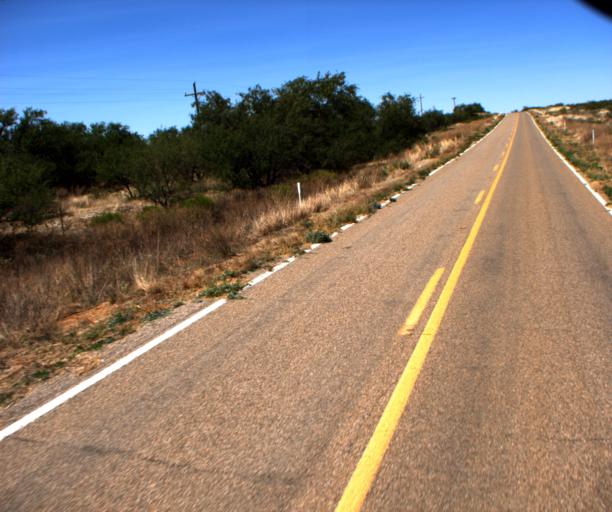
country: US
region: Arizona
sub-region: Santa Cruz County
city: Tubac
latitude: 31.5157
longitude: -111.5434
